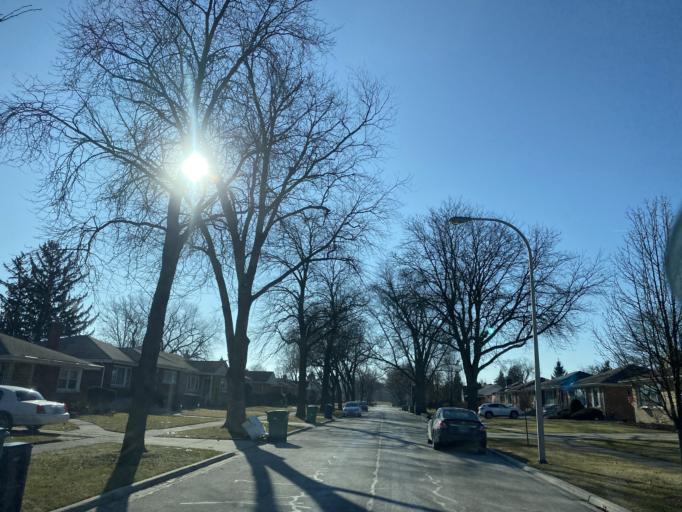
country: US
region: Illinois
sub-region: Cook County
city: Westchester
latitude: 41.8523
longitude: -87.8697
